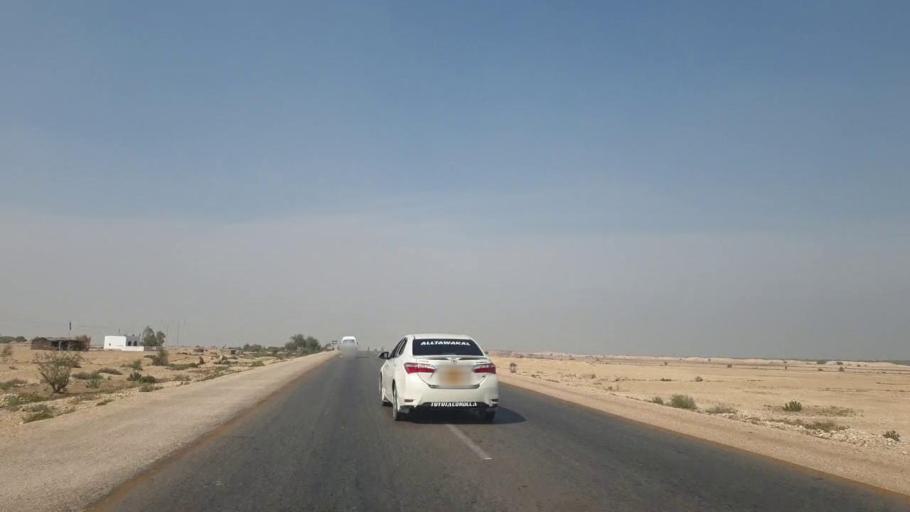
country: PK
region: Sindh
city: Hala
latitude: 25.8418
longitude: 68.2645
